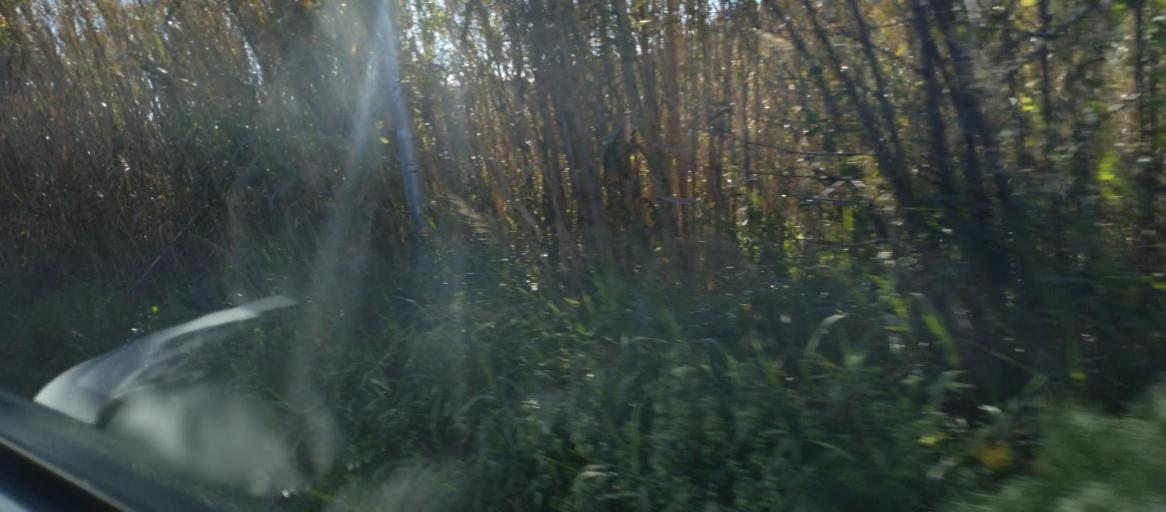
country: IT
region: Calabria
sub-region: Provincia di Catanzaro
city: Catanzaro
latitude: 38.8835
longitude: 16.6036
